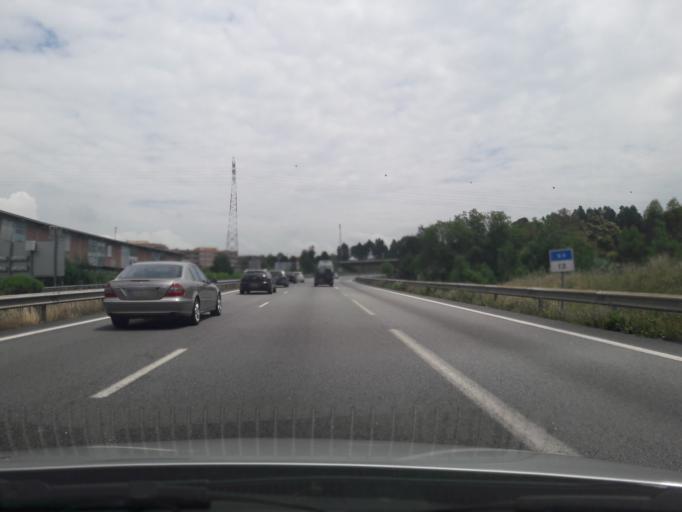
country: PT
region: Porto
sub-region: Gondomar
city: Baguim do Monte
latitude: 41.2027
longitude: -8.5309
